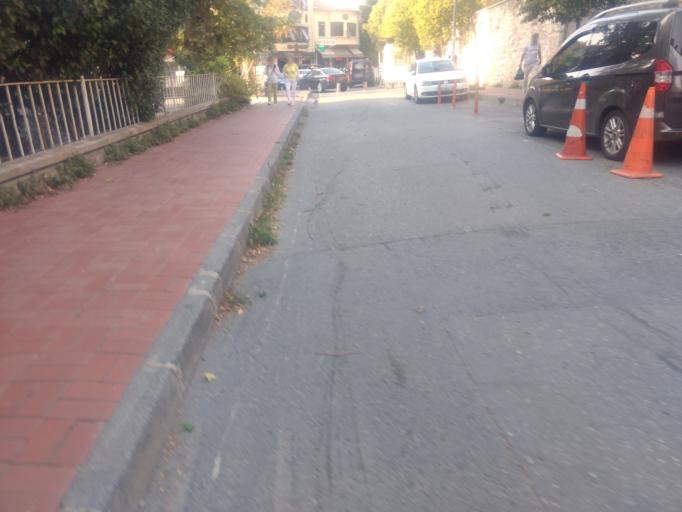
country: TR
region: Istanbul
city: Eminoenue
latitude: 41.0141
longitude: 28.9627
